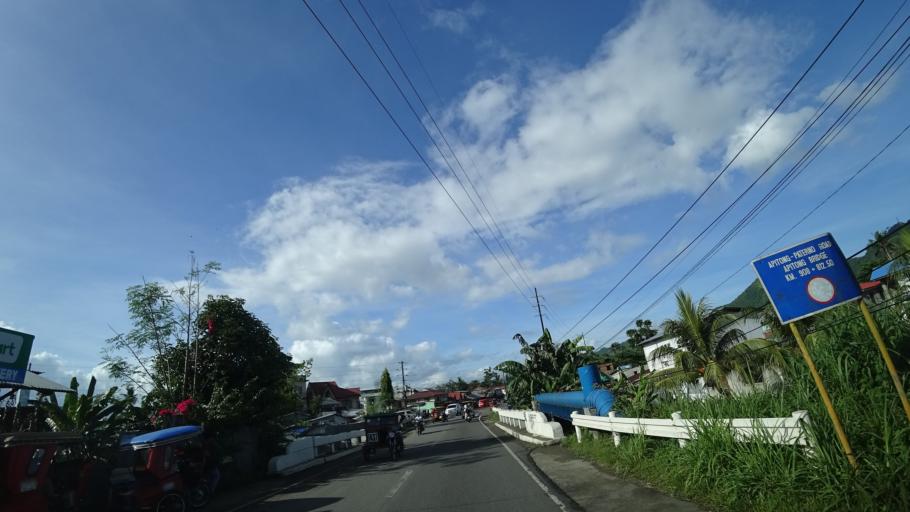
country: PH
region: Eastern Visayas
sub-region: Province of Leyte
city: Panalanoy
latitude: 11.2292
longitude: 124.9984
